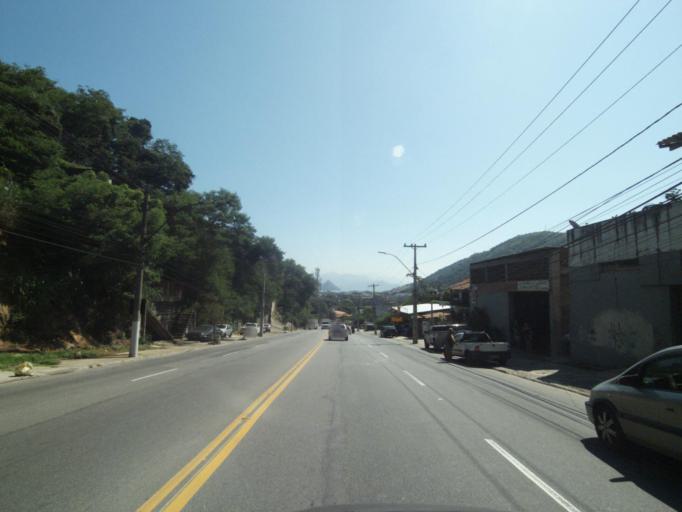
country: BR
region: Rio de Janeiro
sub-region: Niteroi
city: Niteroi
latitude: -22.9120
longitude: -43.0749
